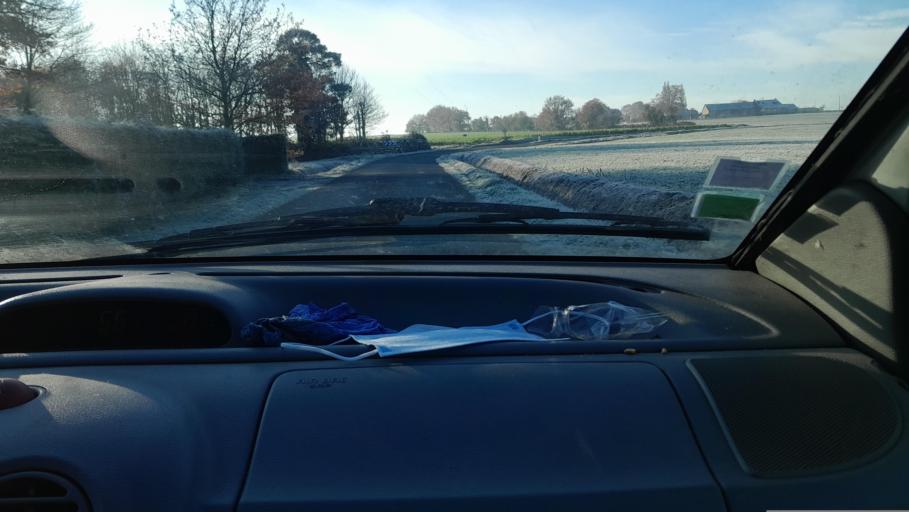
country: FR
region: Brittany
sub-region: Departement d'Ille-et-Vilaine
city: La Guerche-de-Bretagne
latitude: 47.8945
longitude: -1.1630
